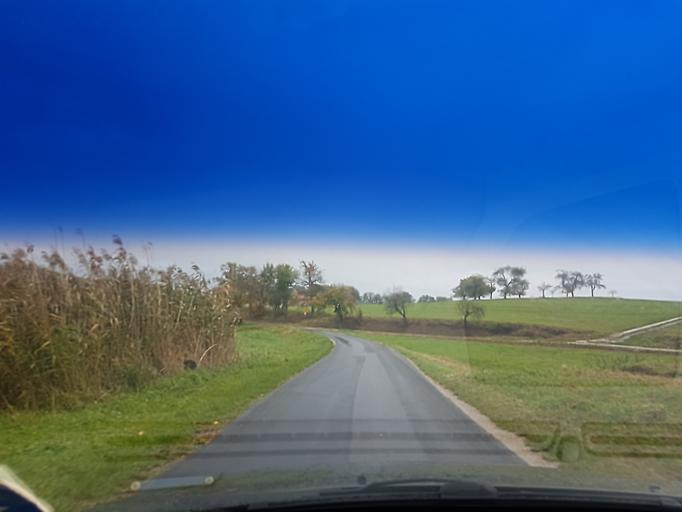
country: DE
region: Bavaria
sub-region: Regierungsbezirk Mittelfranken
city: Wachenroth
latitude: 49.7600
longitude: 10.6866
